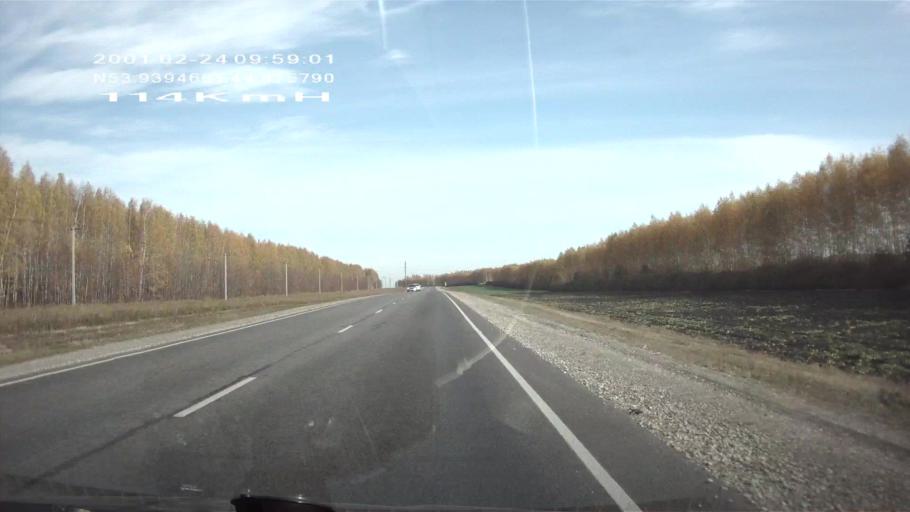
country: RU
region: Penza
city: Issa
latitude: 53.9397
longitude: 44.8760
